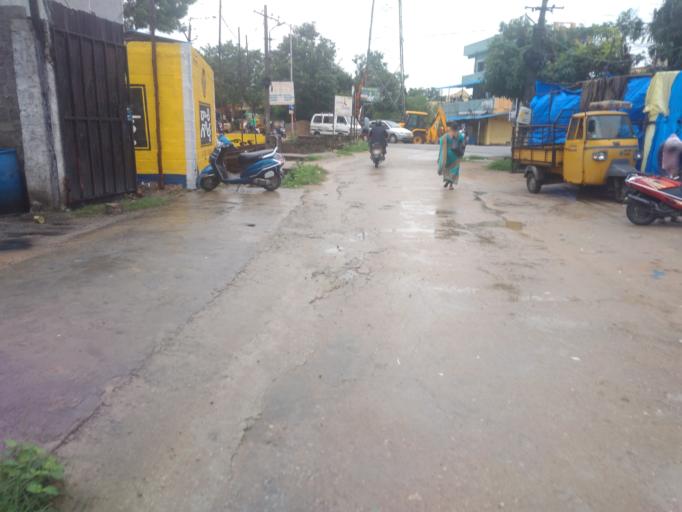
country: IN
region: Telangana
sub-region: Rangareddi
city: Secunderabad
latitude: 17.5102
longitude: 78.5087
